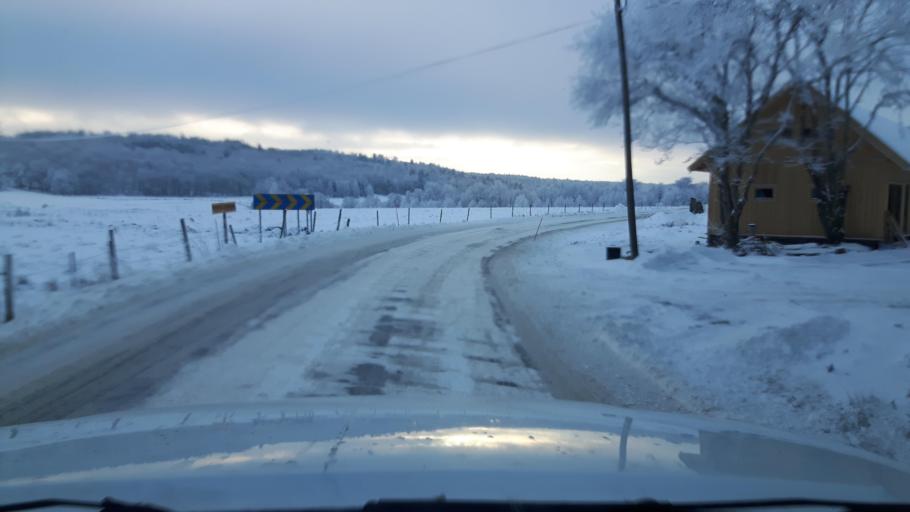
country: SE
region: Halland
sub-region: Kungsbacka Kommun
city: Frillesas
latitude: 57.3329
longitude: 12.2487
